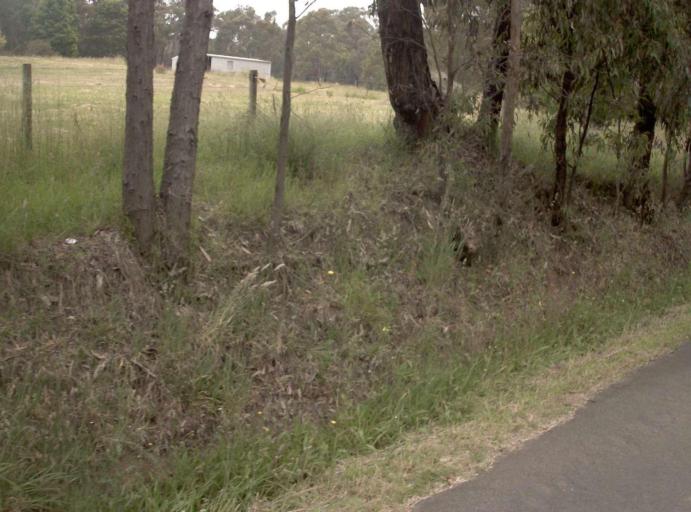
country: AU
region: Victoria
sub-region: Latrobe
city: Moe
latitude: -38.3758
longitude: 146.1776
